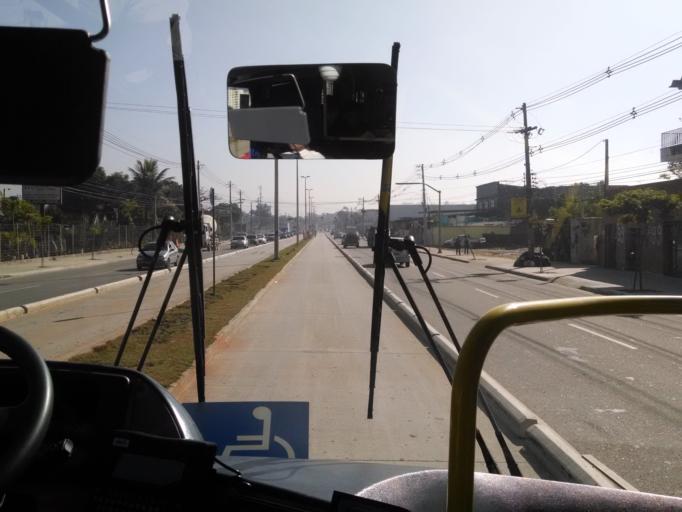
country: BR
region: Rio de Janeiro
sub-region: Nilopolis
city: Nilopolis
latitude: -22.9658
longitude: -43.3903
